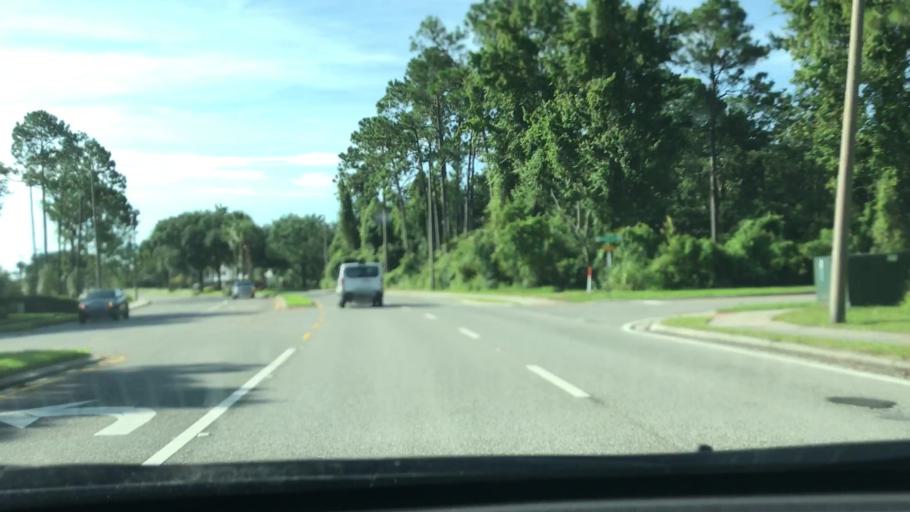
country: US
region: Florida
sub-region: Orange County
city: Williamsburg
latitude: 28.3978
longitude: -81.4741
